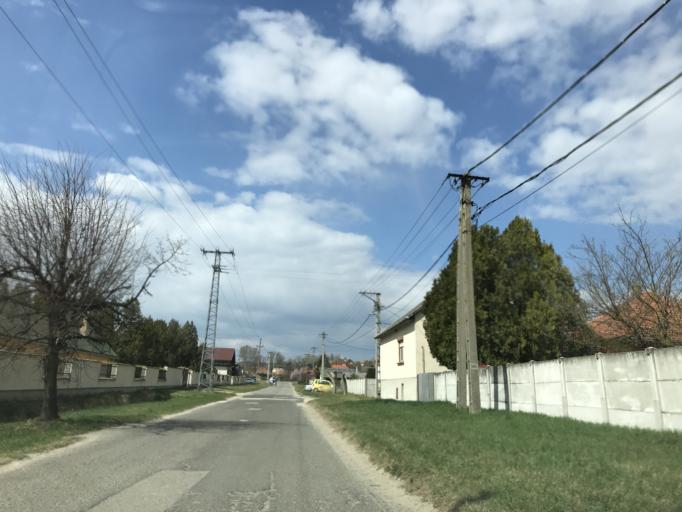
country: HU
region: Komarom-Esztergom
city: Kesztolc
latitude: 47.7101
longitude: 18.7847
